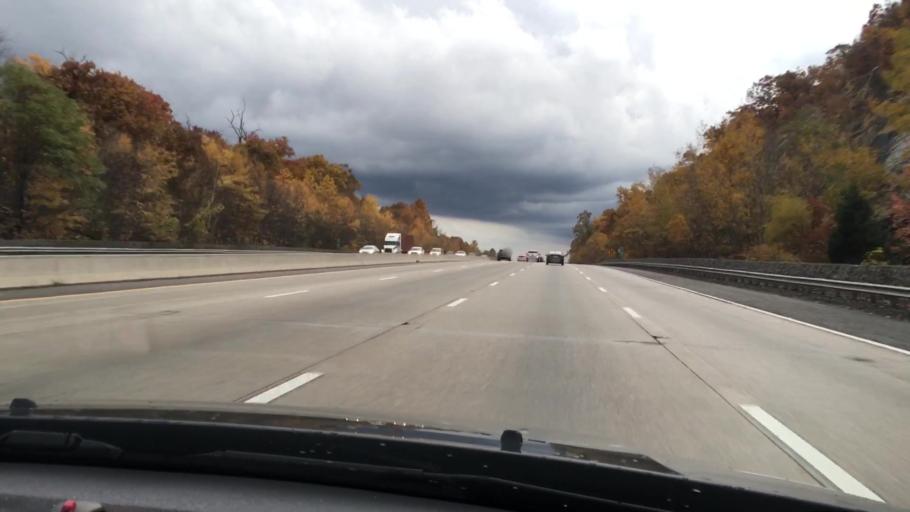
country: US
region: New Jersey
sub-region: Passaic County
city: Bloomingdale
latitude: 40.9573
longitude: -74.3384
